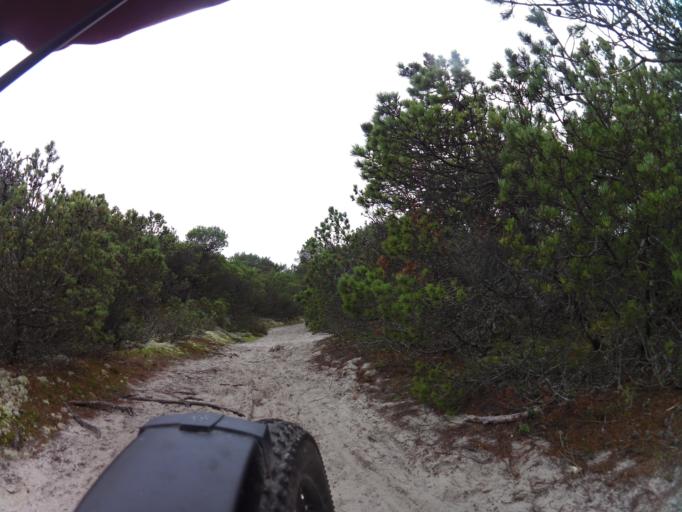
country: PL
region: Pomeranian Voivodeship
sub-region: Powiat pucki
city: Hel
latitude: 54.6276
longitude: 18.8172
